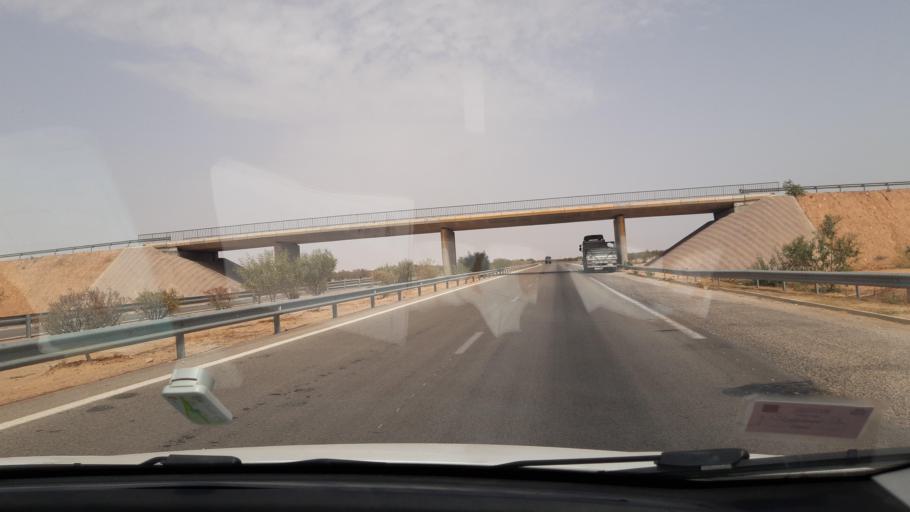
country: TN
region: Safaqis
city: Bi'r `Ali Bin Khalifah
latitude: 34.5436
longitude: 10.3081
